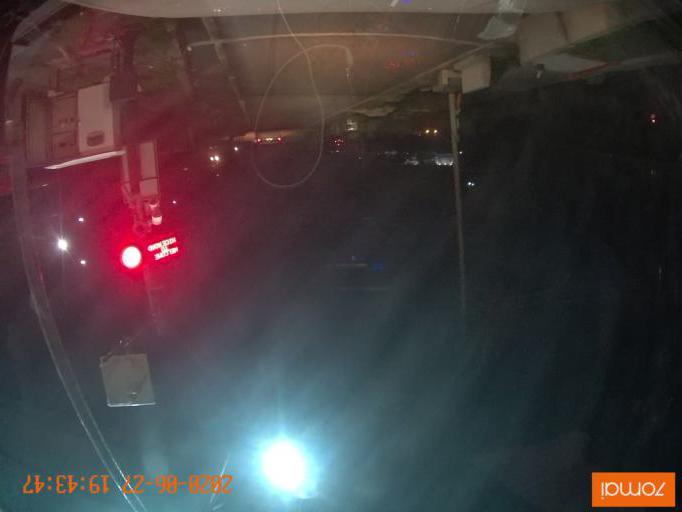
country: IN
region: Karnataka
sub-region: Bangalore Urban
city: Bangalore
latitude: 12.8499
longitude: 77.5908
